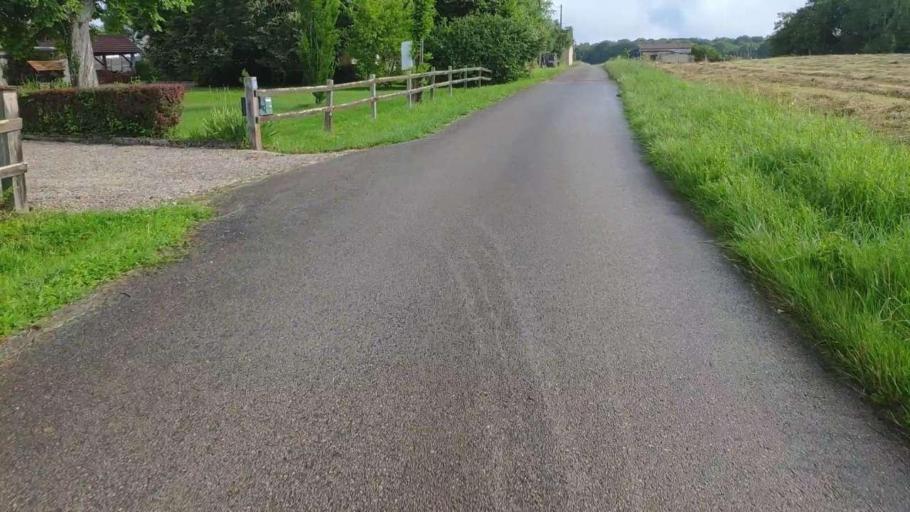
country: FR
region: Franche-Comte
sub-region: Departement du Jura
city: Mont-sous-Vaudrey
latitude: 46.8747
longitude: 5.5223
